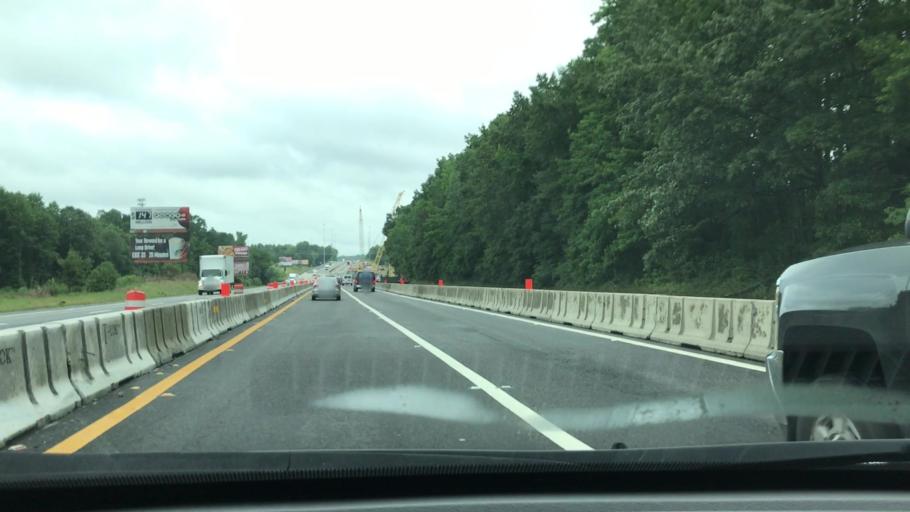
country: US
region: Virginia
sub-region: City of Emporia
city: Emporia
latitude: 36.6912
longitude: -77.5558
